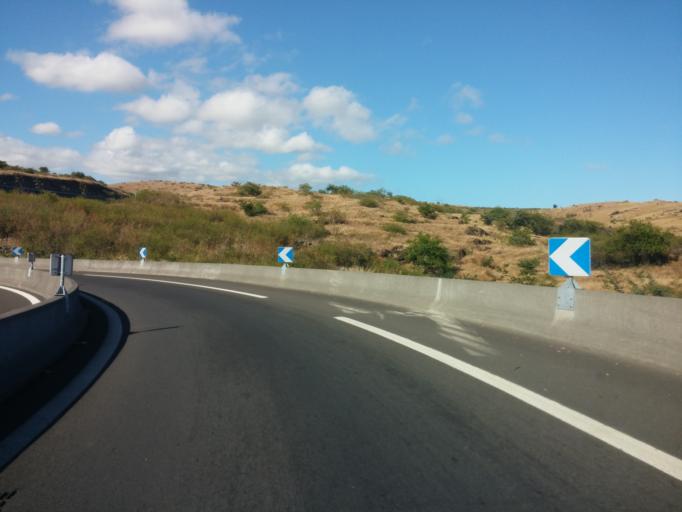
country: RE
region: Reunion
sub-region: Reunion
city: Saint-Paul
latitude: -21.0211
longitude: 55.2554
